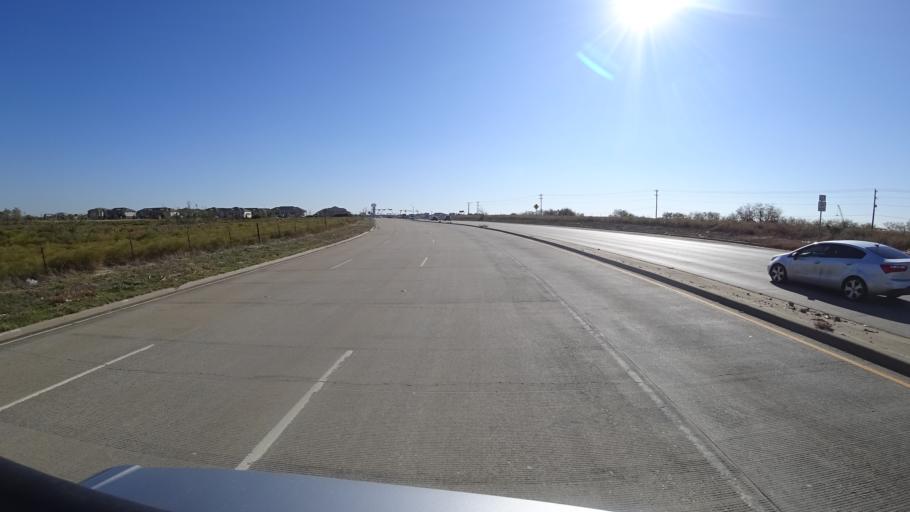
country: US
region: Texas
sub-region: Denton County
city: The Colony
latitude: 33.0474
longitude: -96.9261
